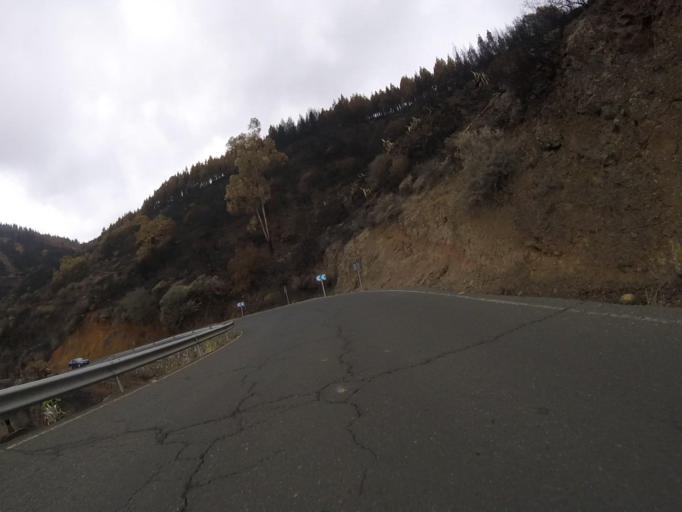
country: ES
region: Canary Islands
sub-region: Provincia de Las Palmas
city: Tejeda
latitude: 27.9856
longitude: -15.5762
